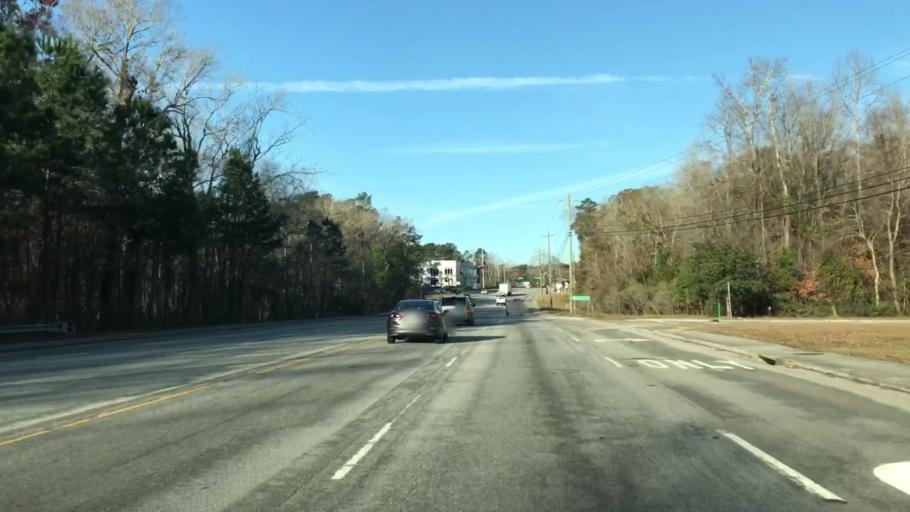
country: US
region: South Carolina
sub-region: Berkeley County
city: Ladson
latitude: 32.9807
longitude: -80.0838
